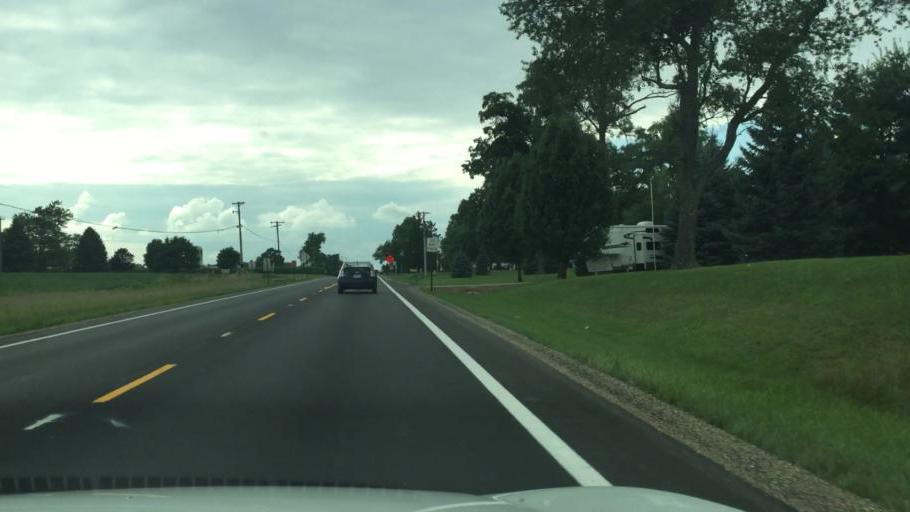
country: US
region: Ohio
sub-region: Champaign County
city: Urbana
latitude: 40.0905
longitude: -83.6930
